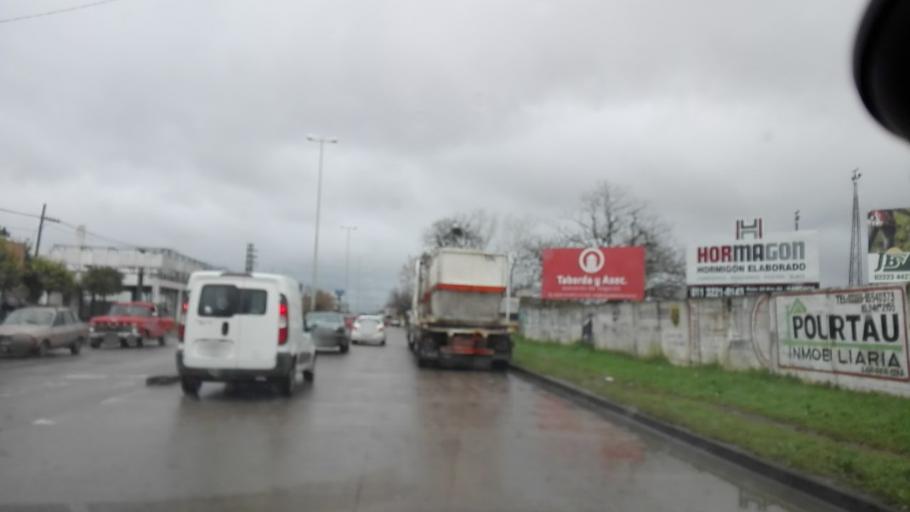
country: AR
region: Buenos Aires
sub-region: Partido de Brandsen
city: Brandsen
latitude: -35.1741
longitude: -58.2331
